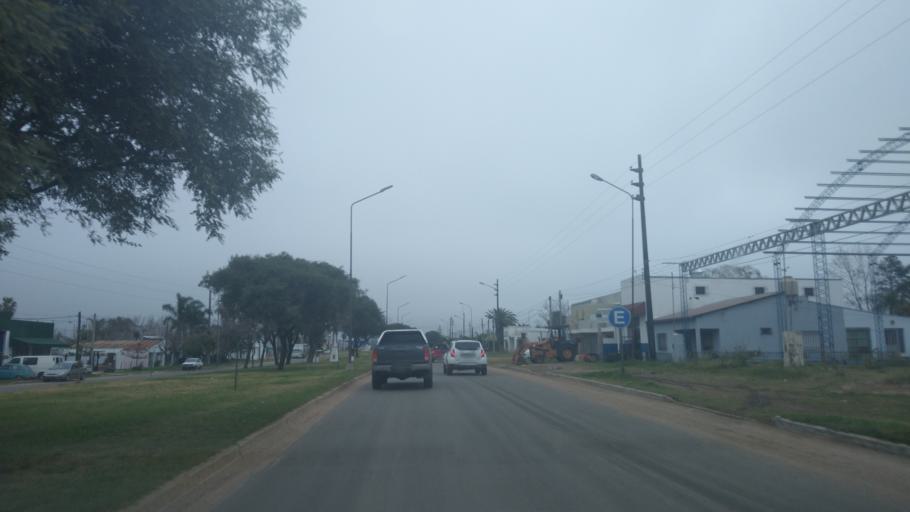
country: AR
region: Entre Rios
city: Chajari
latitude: -30.7613
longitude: -58.0064
